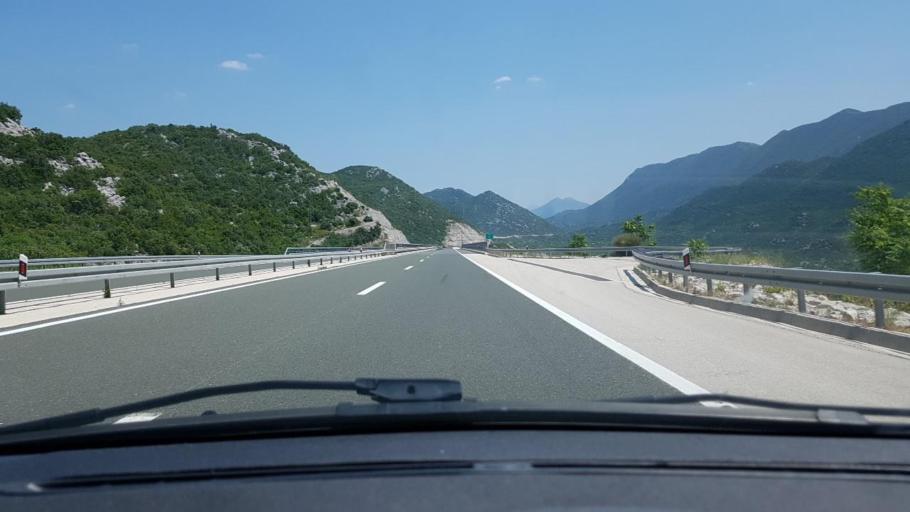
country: HR
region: Splitsko-Dalmatinska
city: Vrgorac
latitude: 43.2037
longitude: 17.3144
